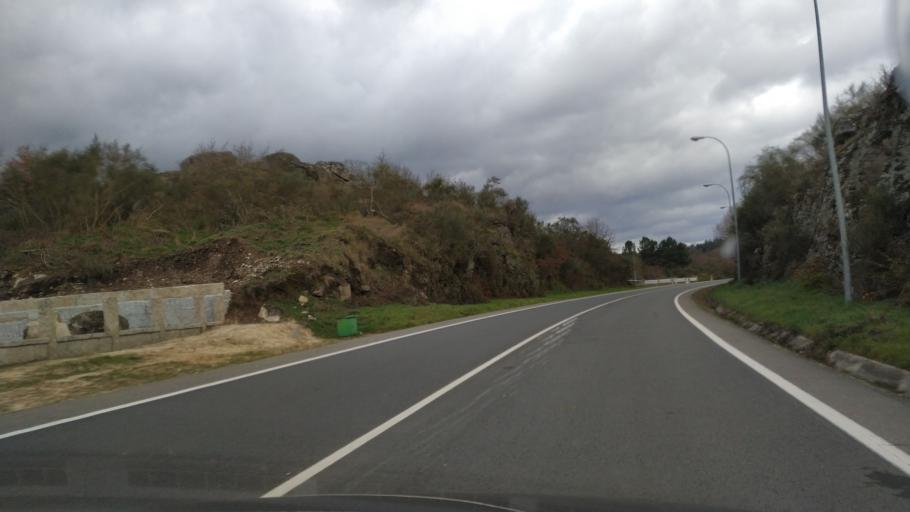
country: ES
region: Galicia
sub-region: Provincia de Ourense
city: Allariz
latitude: 42.1946
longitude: -7.7974
